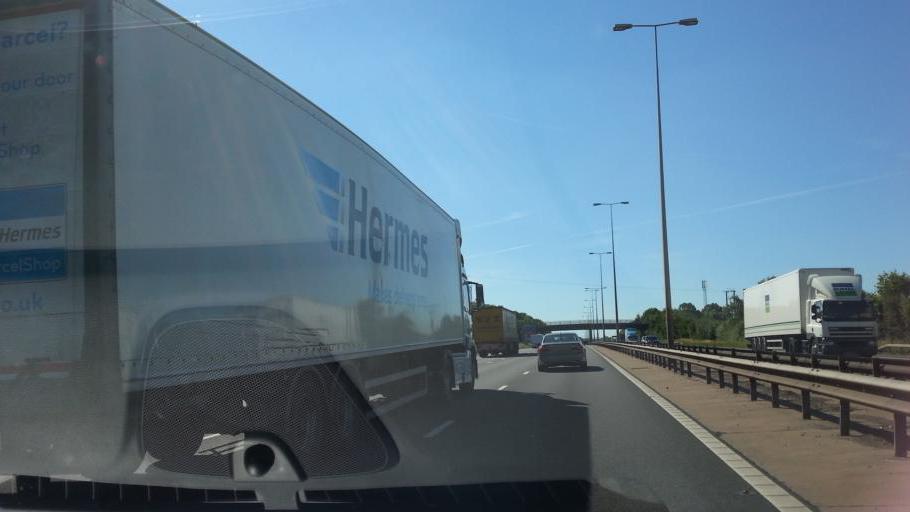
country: GB
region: England
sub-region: Worcestershire
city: Upton upon Severn
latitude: 52.0734
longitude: -2.1639
